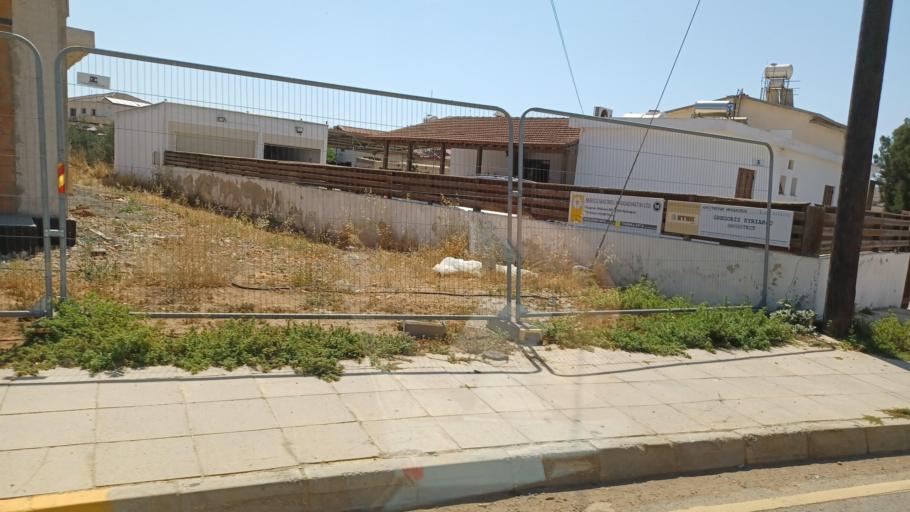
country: CY
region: Ammochostos
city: Liopetri
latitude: 35.0115
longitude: 33.8913
